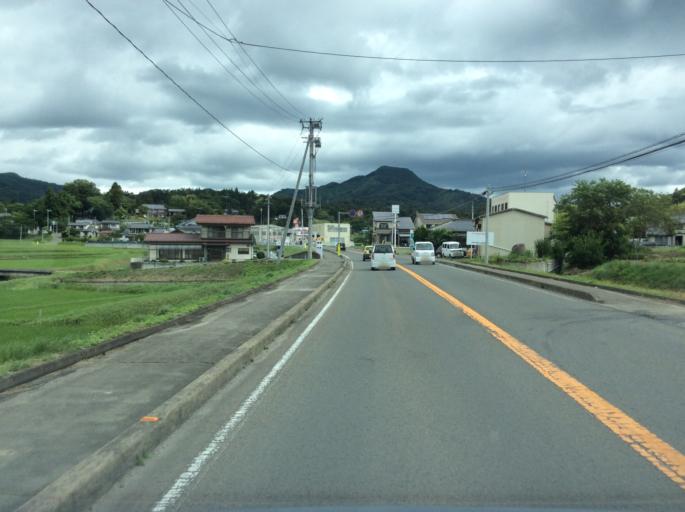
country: JP
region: Fukushima
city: Fukushima-shi
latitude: 37.6791
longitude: 140.5650
